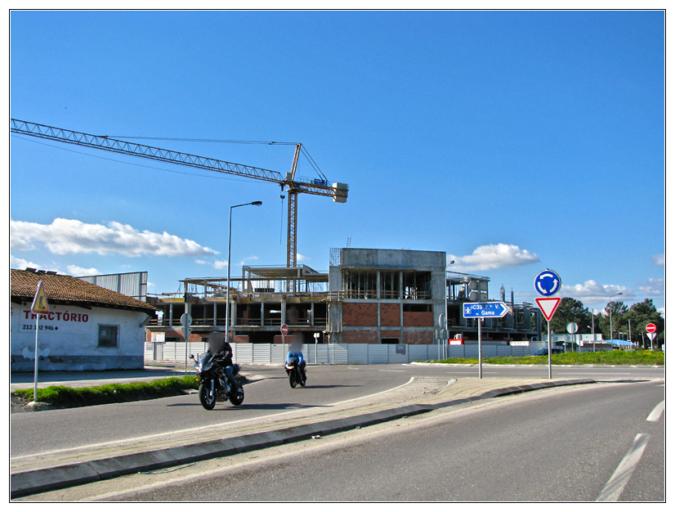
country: PT
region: Setubal
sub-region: Barreiro
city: Santo Antonio da Charneca
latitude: 38.5966
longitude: -9.0512
